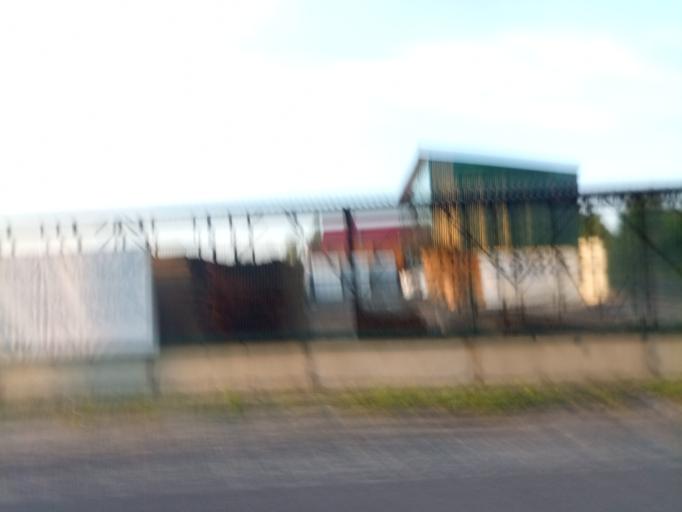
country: RU
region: Moskovskaya
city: Noginsk-9
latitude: 56.1084
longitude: 38.6226
